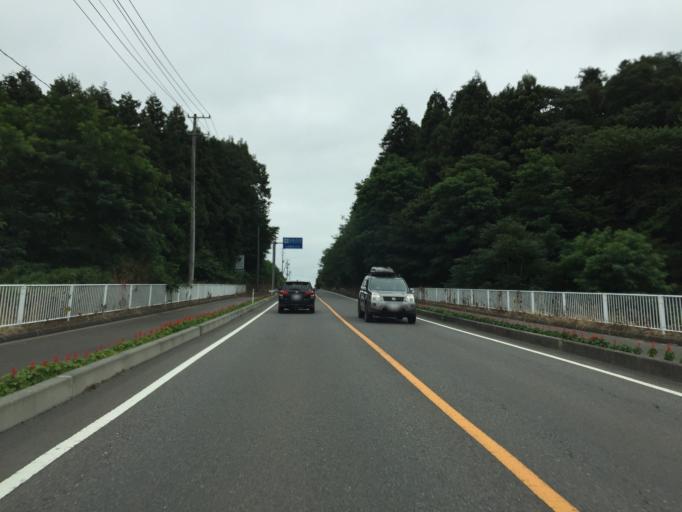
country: JP
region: Fukushima
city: Sukagawa
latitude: 37.2384
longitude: 140.3965
